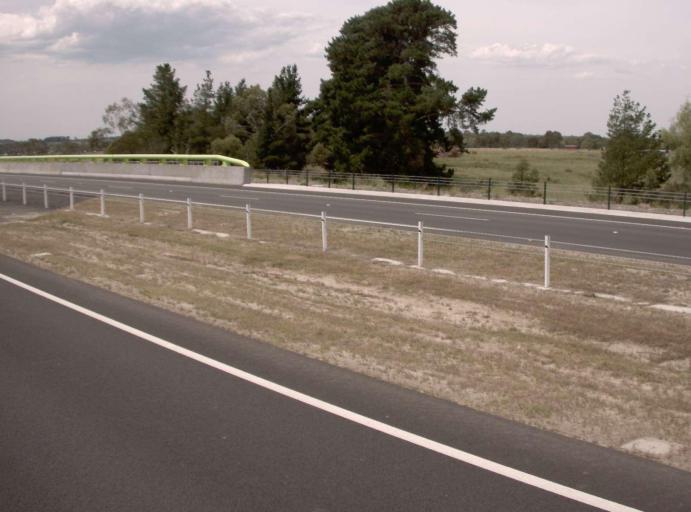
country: AU
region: Victoria
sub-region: Mornington Peninsula
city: Moorooduc
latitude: -38.2086
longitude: 145.1314
